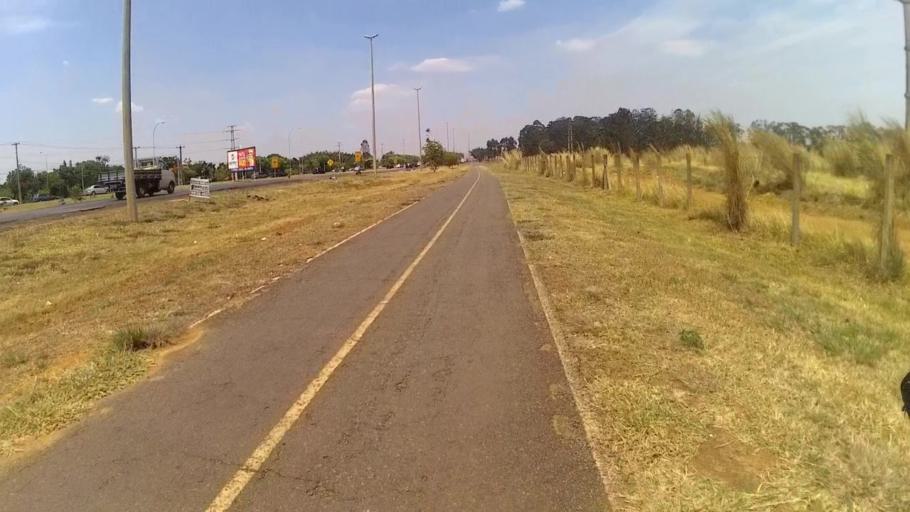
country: BR
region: Federal District
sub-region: Brasilia
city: Brasilia
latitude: -15.8750
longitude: -48.0482
